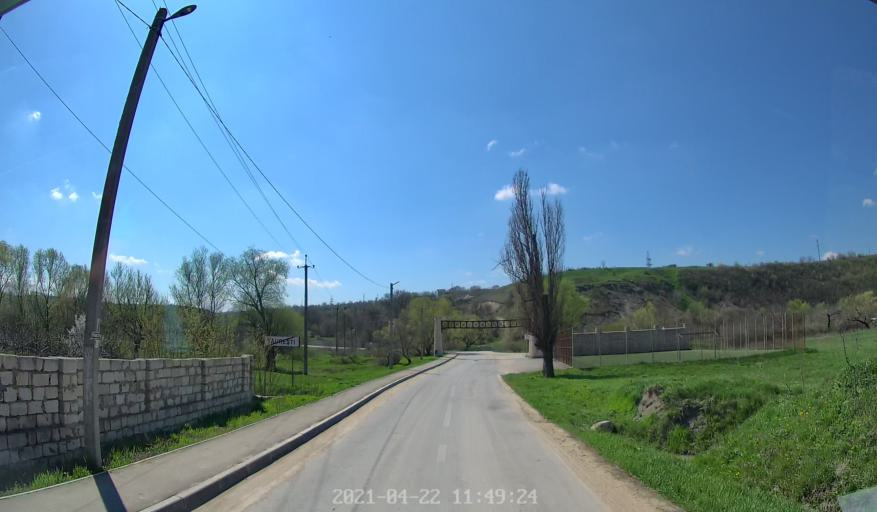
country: MD
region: Chisinau
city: Ciorescu
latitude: 47.1424
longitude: 28.8974
